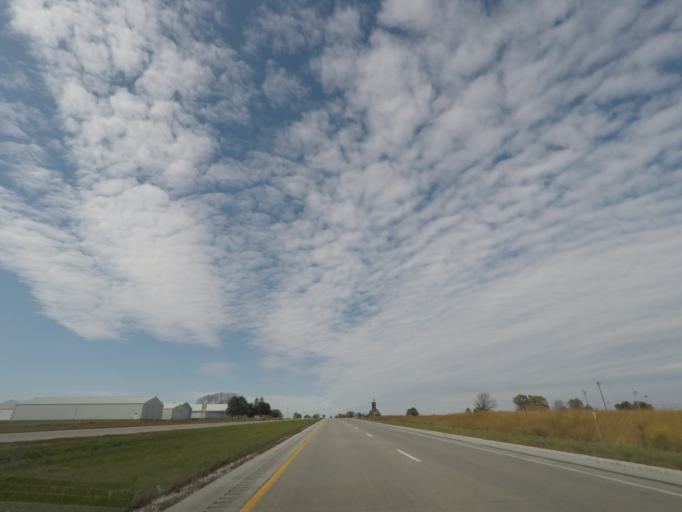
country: US
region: Iowa
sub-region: Boone County
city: Boone
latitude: 42.0234
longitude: -93.7727
